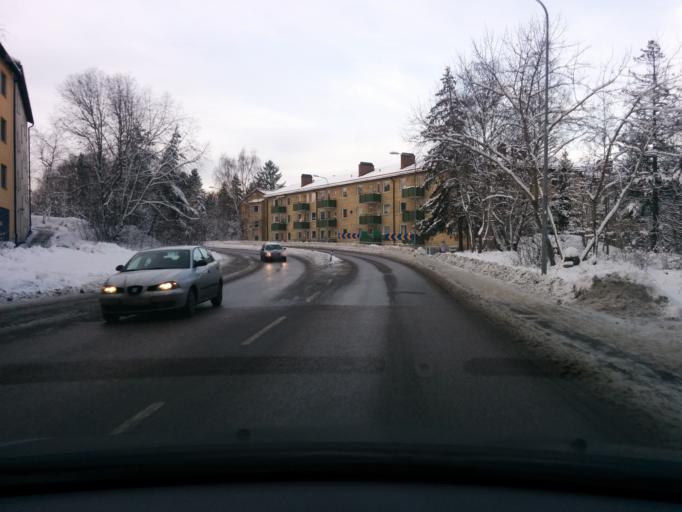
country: SE
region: Stockholm
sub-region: Stockholms Kommun
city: Arsta
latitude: 59.2710
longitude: 18.0471
